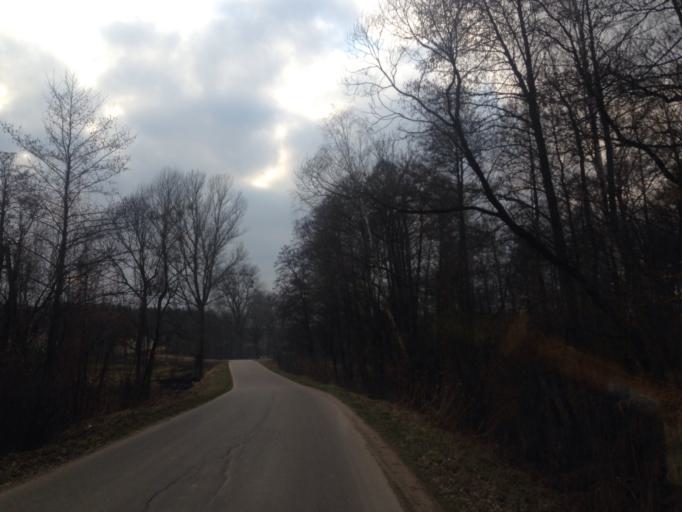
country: PL
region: Warmian-Masurian Voivodeship
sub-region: Powiat dzialdowski
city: Lidzbark
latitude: 53.3483
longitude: 19.7479
